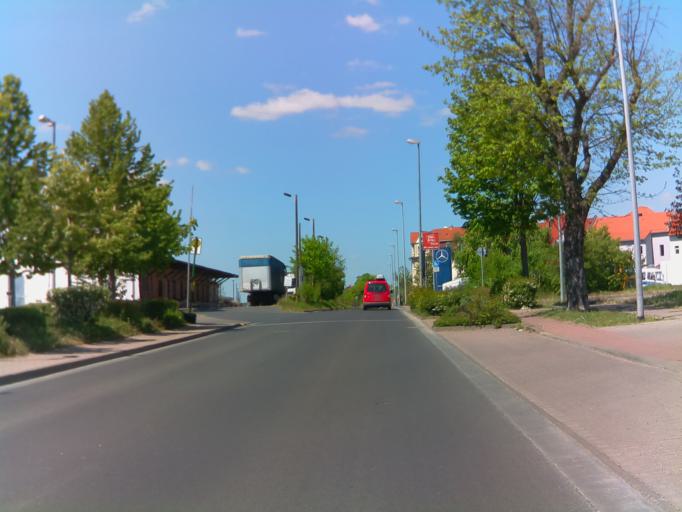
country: DE
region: Thuringia
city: Arnstadt
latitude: 50.8417
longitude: 10.9501
